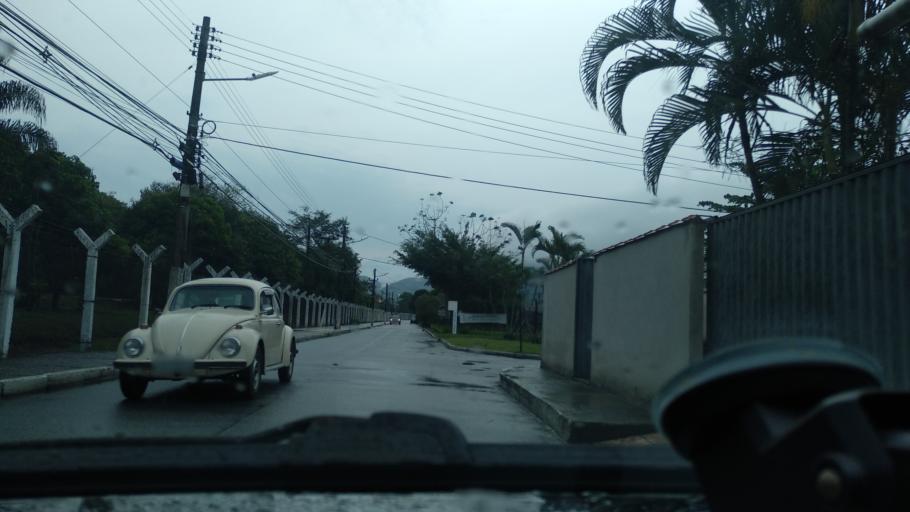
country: BR
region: Rio de Janeiro
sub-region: Angra Dos Reis
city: Angra dos Reis
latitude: -23.0309
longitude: -44.5475
